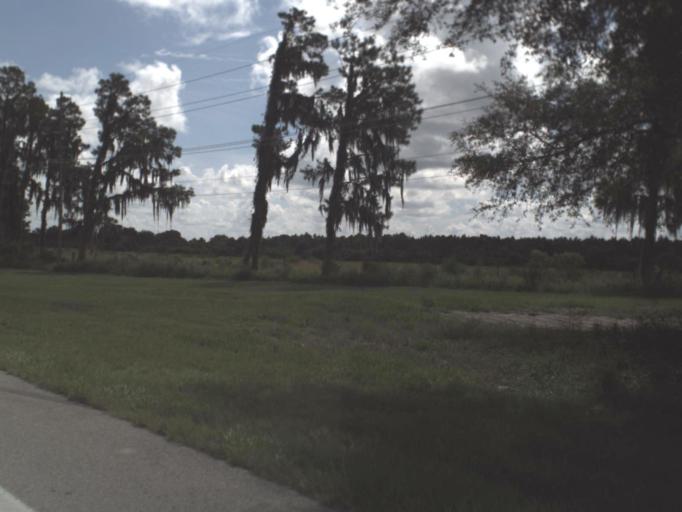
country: US
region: Florida
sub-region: Polk County
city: Combee Settlement
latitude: 28.1115
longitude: -81.9158
